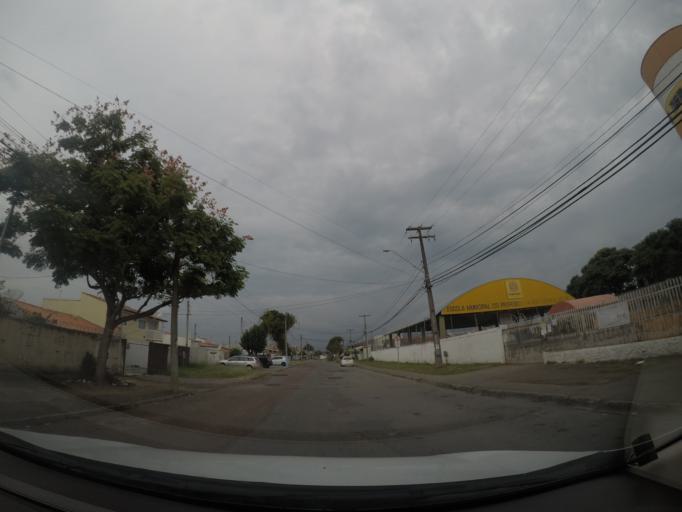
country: BR
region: Parana
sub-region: Sao Jose Dos Pinhais
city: Sao Jose dos Pinhais
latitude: -25.5240
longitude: -49.2334
